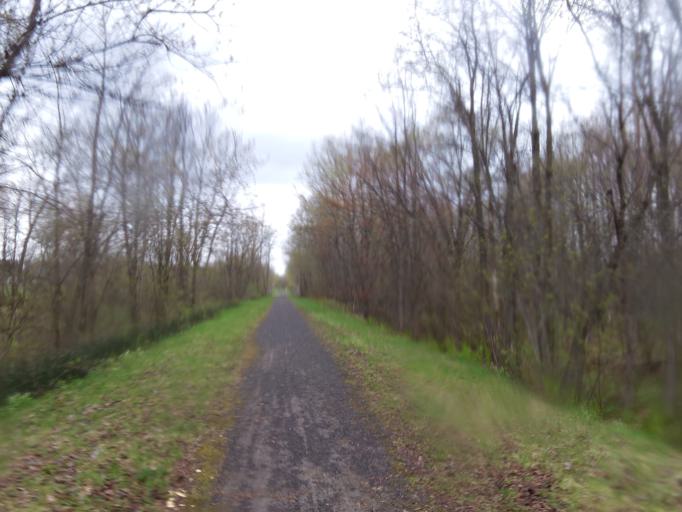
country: CA
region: Ontario
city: Bourget
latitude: 45.4374
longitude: -75.2194
